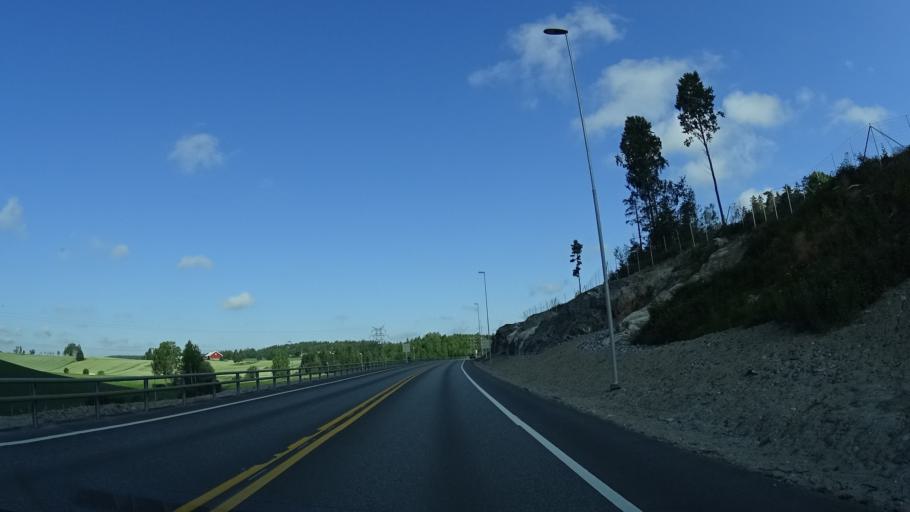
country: NO
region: Ostfold
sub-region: Hobol
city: Elvestad
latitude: 59.6450
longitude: 10.9265
